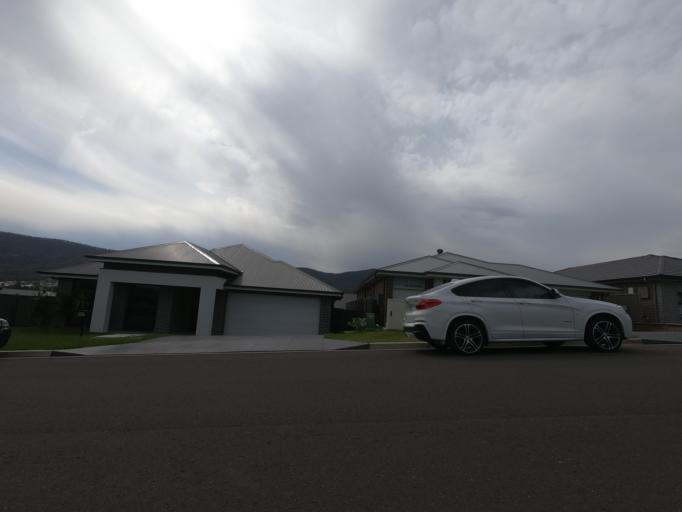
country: AU
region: New South Wales
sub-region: Wollongong
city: Dapto
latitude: -34.4804
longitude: 150.7835
